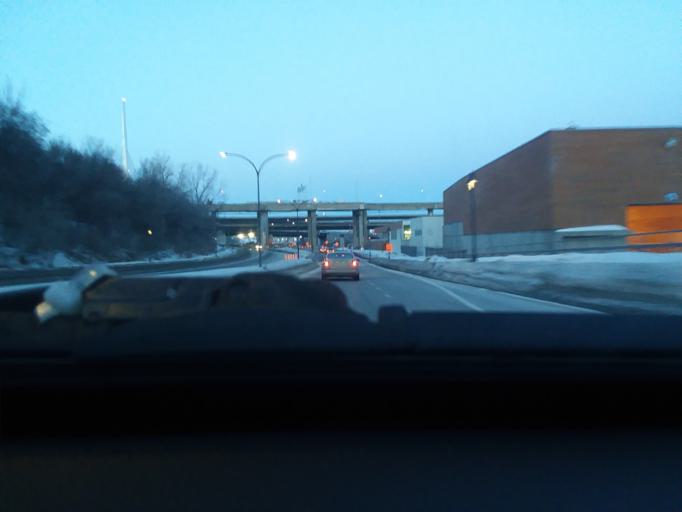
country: CA
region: Quebec
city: Saint-Raymond
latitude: 45.4674
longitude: -73.6052
